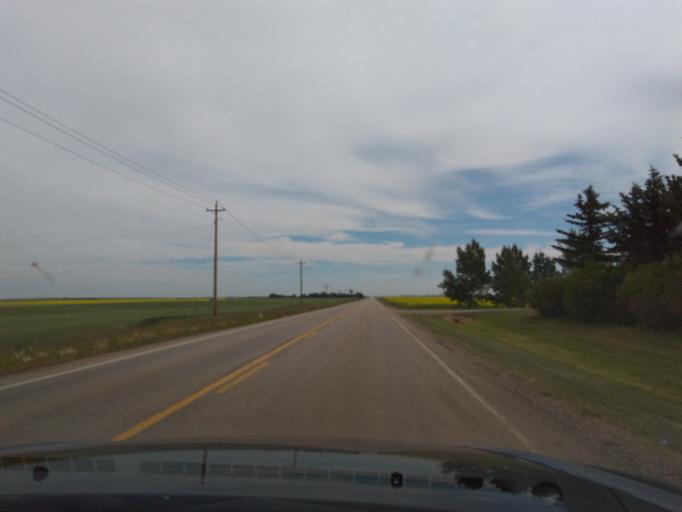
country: CA
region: Alberta
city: Three Hills
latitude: 51.5033
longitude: -113.0052
